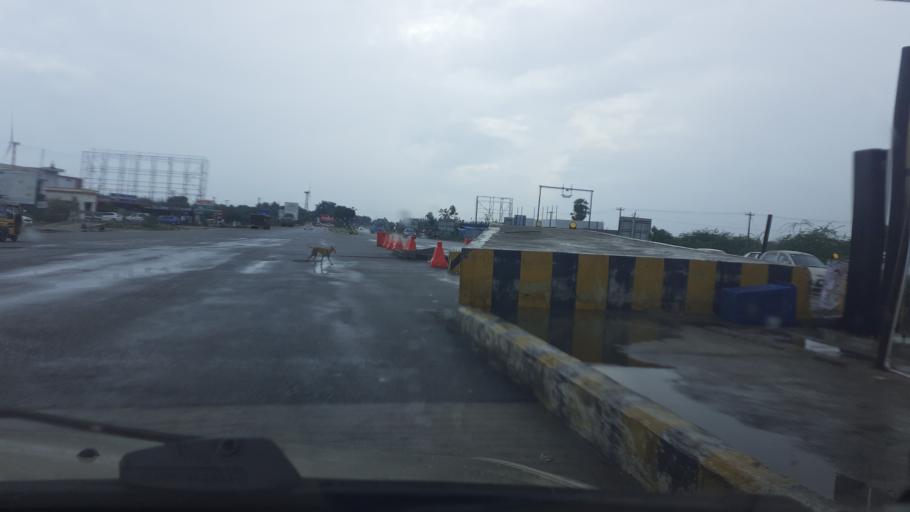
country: IN
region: Tamil Nadu
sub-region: Thoothukkudi
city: Kayattar
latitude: 8.9755
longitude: 77.7747
